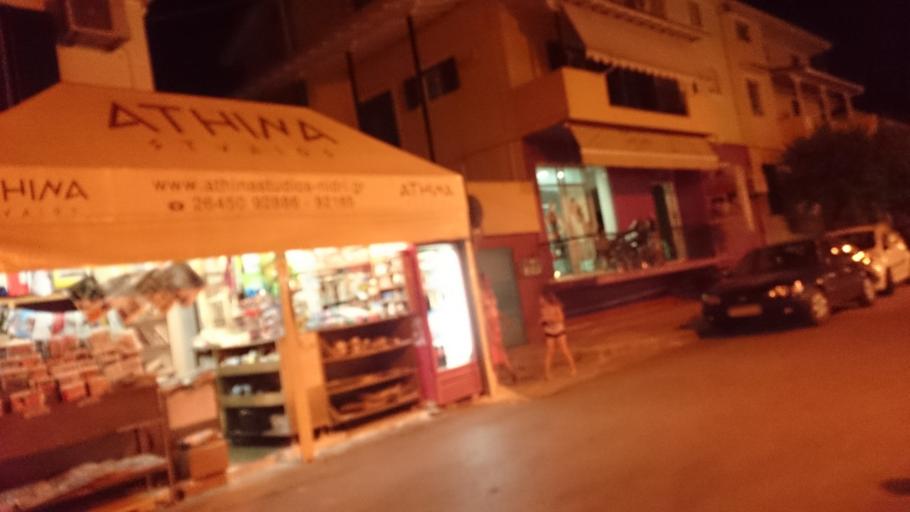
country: GR
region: Ionian Islands
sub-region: Lefkada
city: Nidri
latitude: 38.7051
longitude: 20.7083
